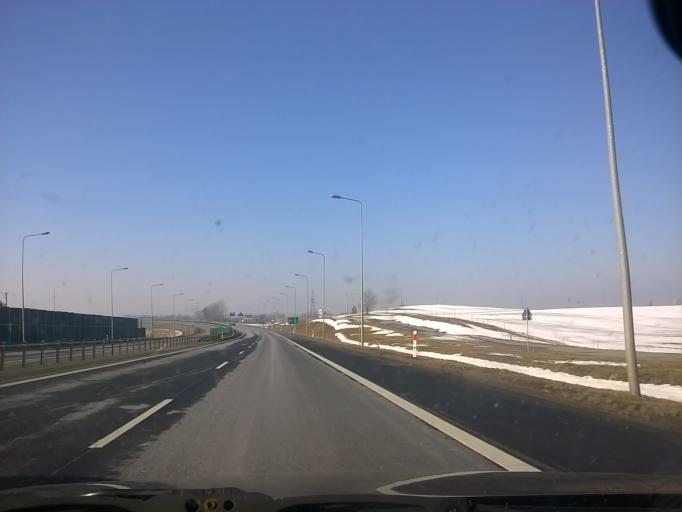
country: PL
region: Warmian-Masurian Voivodeship
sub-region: Powiat olsztynski
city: Biskupiec
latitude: 53.8477
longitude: 20.9778
